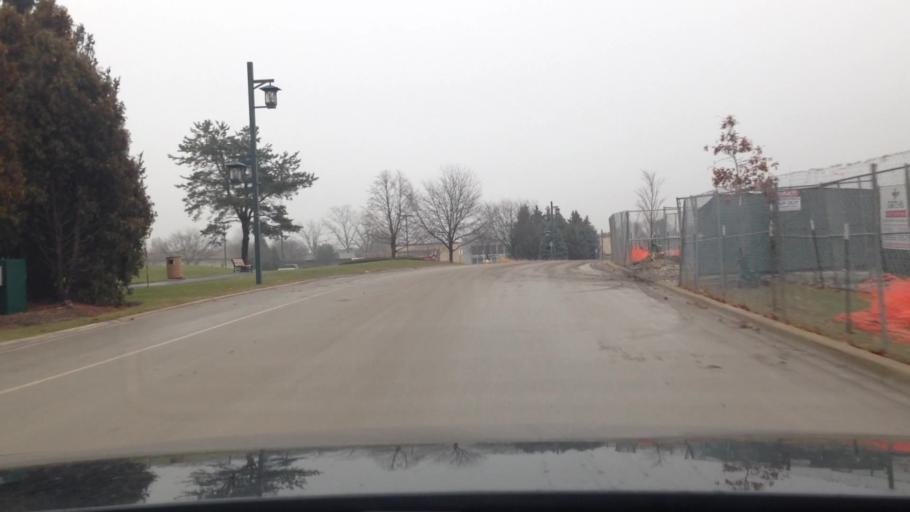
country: US
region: Illinois
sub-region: DuPage County
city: Westmont
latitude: 41.8131
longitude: -87.9707
